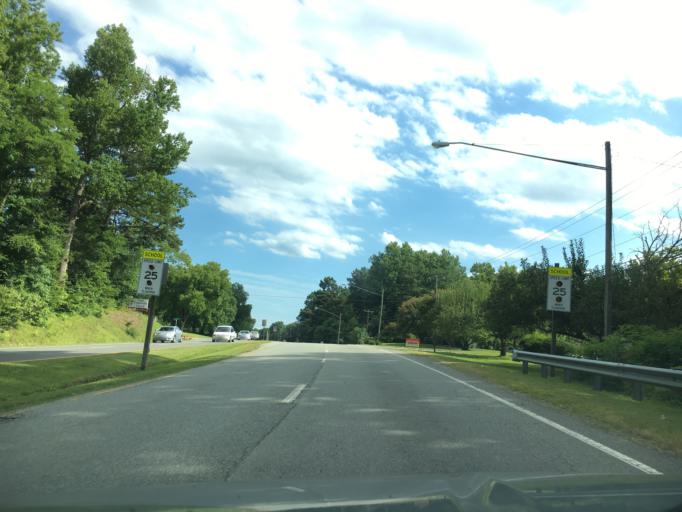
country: US
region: Virginia
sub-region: Halifax County
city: South Boston
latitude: 36.7270
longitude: -78.9190
